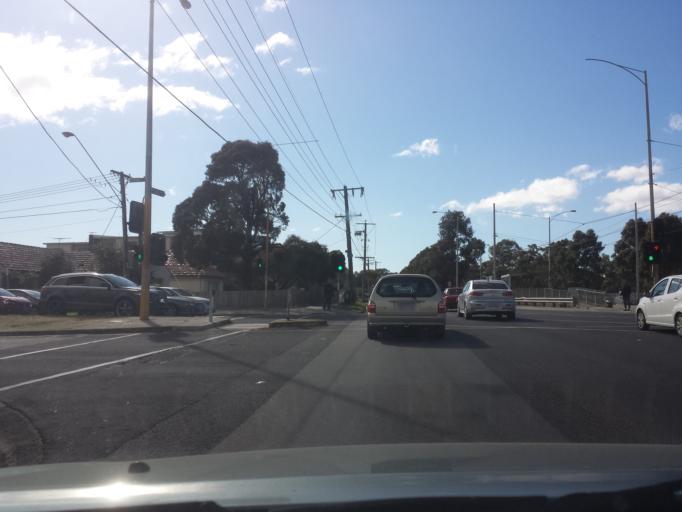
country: AU
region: Victoria
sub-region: Darebin
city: Kingsbury
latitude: -37.7170
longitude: 145.0428
